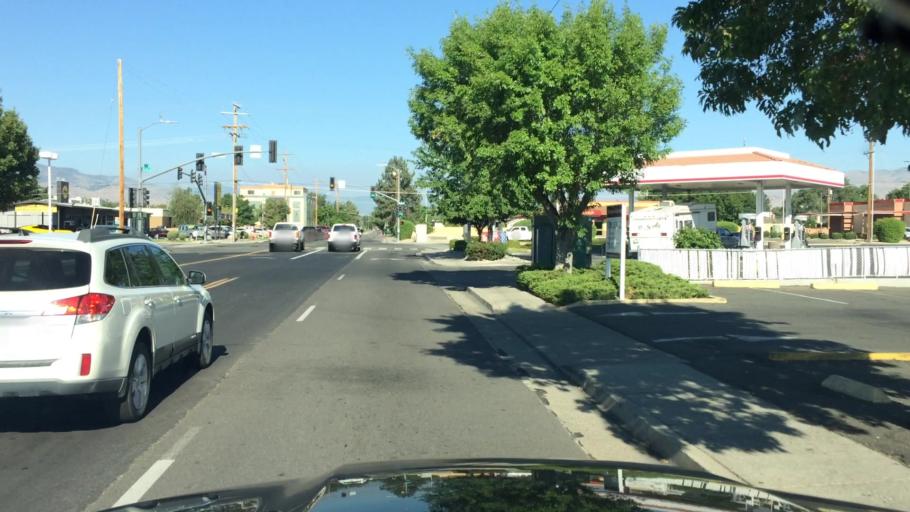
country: US
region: Nevada
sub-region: Washoe County
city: Reno
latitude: 39.5131
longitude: -119.7882
